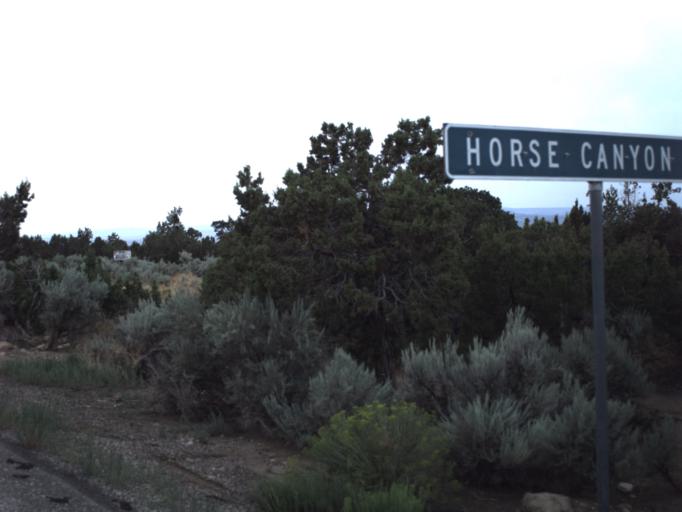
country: US
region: Utah
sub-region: Carbon County
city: East Carbon City
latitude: 39.5426
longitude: -110.4144
